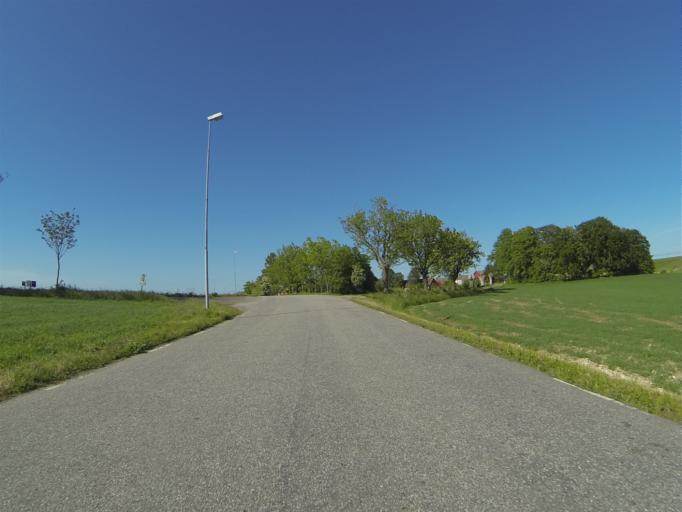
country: SE
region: Skane
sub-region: Malmo
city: Oxie
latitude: 55.5964
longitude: 13.1328
